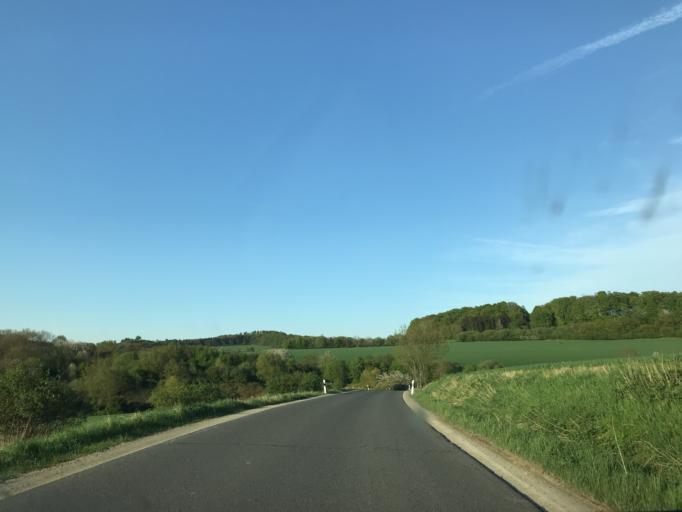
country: DE
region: Thuringia
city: Heuthen
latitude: 51.3372
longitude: 10.2340
